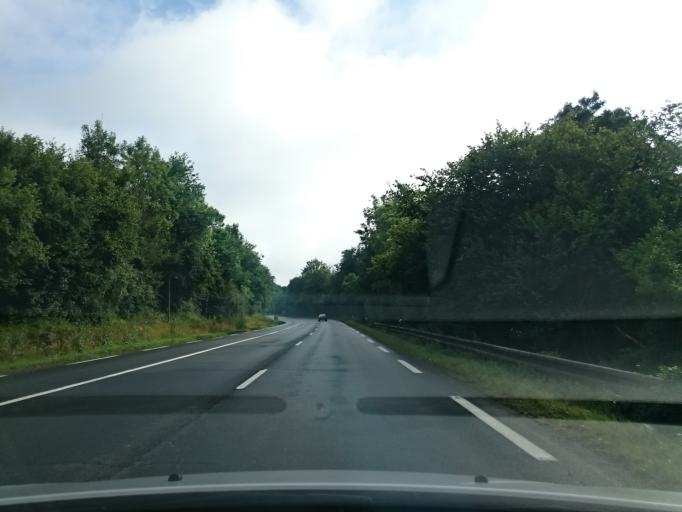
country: FR
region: Lower Normandy
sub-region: Departement du Calvados
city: Cambremer
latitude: 49.1262
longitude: 0.1040
